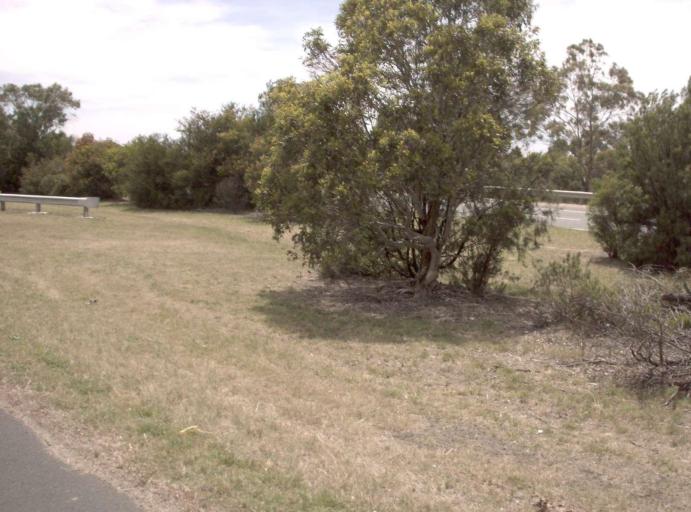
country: AU
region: Victoria
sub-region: Casey
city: Hampton Park
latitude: -38.0374
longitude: 145.2468
